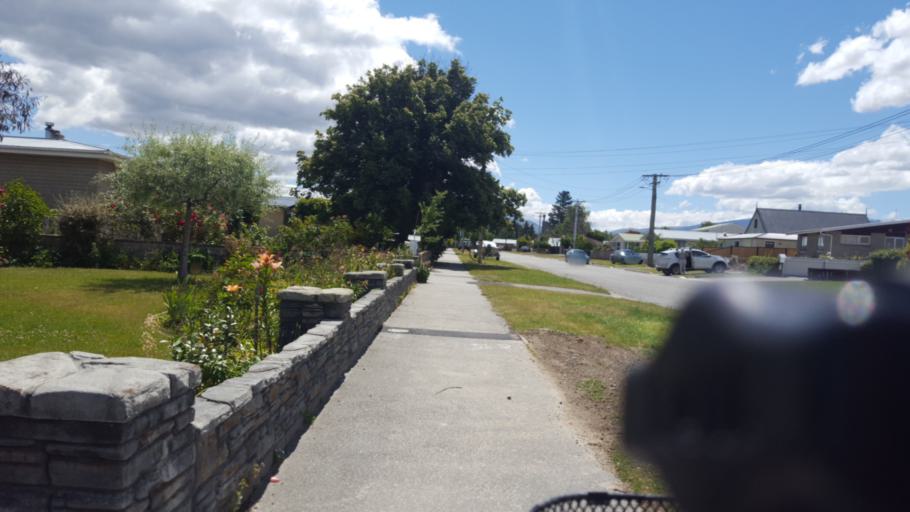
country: NZ
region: Otago
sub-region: Queenstown-Lakes District
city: Wanaka
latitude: -45.2429
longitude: 169.3904
